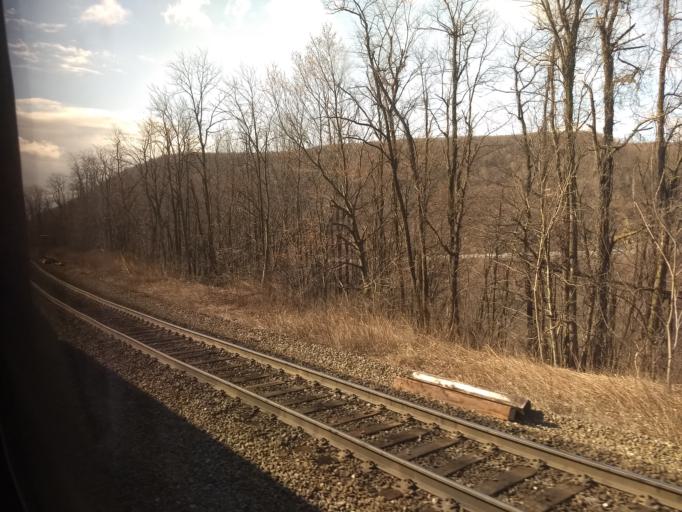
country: US
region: Pennsylvania
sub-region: Cambria County
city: Gallitzin
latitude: 40.4776
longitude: -78.4936
